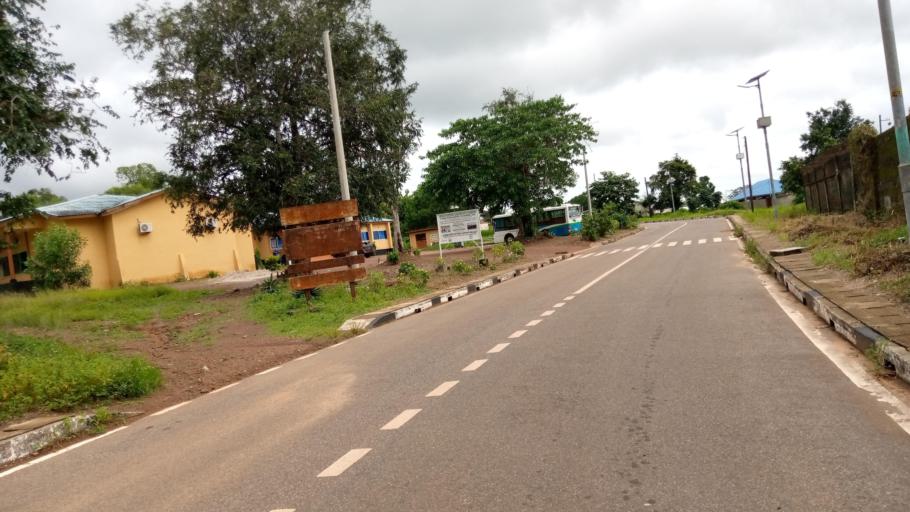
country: SL
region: Southern Province
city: Moyamba
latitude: 8.1615
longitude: -12.4390
